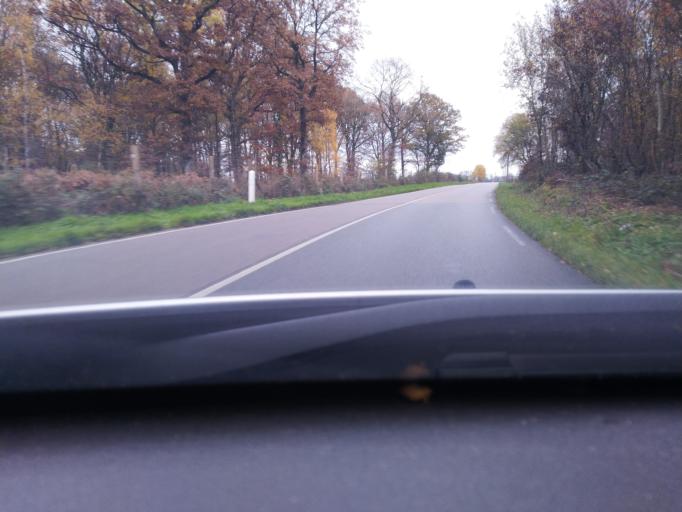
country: FR
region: Haute-Normandie
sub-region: Departement de la Seine-Maritime
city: Saint-Pierre-de-Varengeville
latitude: 49.4974
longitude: 0.9116
